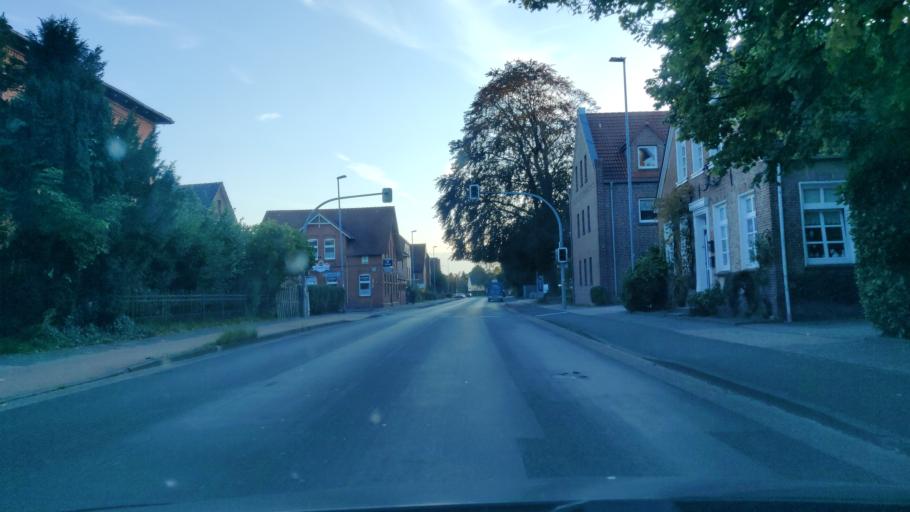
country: DE
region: Lower Saxony
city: Aurich
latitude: 53.4674
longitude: 7.4711
